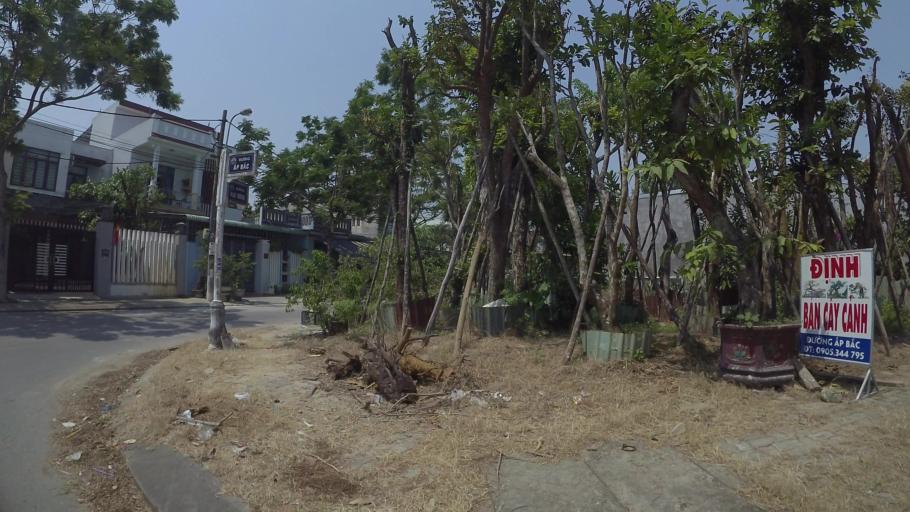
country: VN
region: Da Nang
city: Ngu Hanh Son
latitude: 15.9929
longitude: 108.2574
